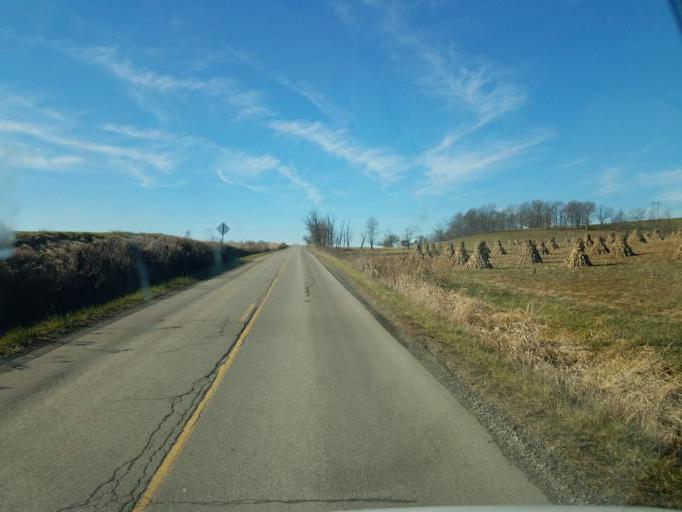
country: US
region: Ohio
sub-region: Wayne County
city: Dalton
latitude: 40.7338
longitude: -81.7150
